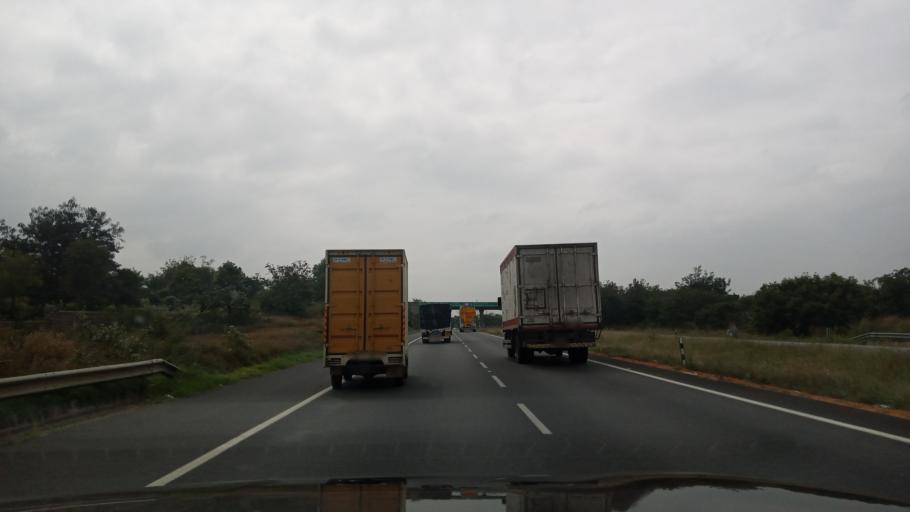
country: IN
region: Karnataka
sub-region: Bangalore Urban
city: Bangalore
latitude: 12.9167
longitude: 77.4682
